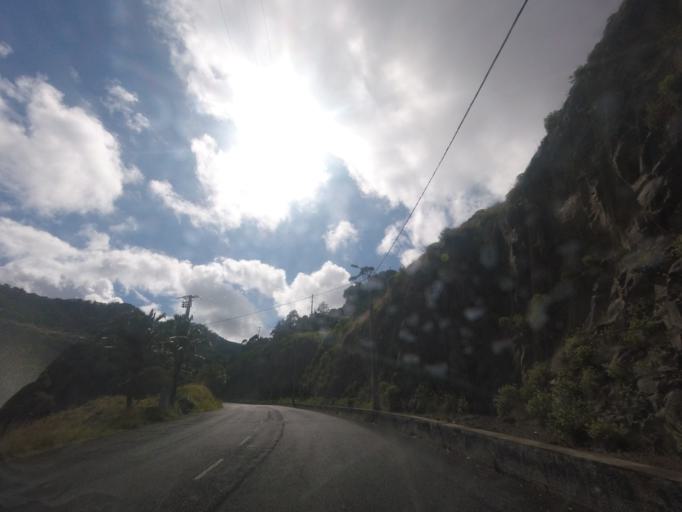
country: PT
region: Madeira
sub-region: Machico
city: Canical
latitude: 32.7384
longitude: -16.7534
